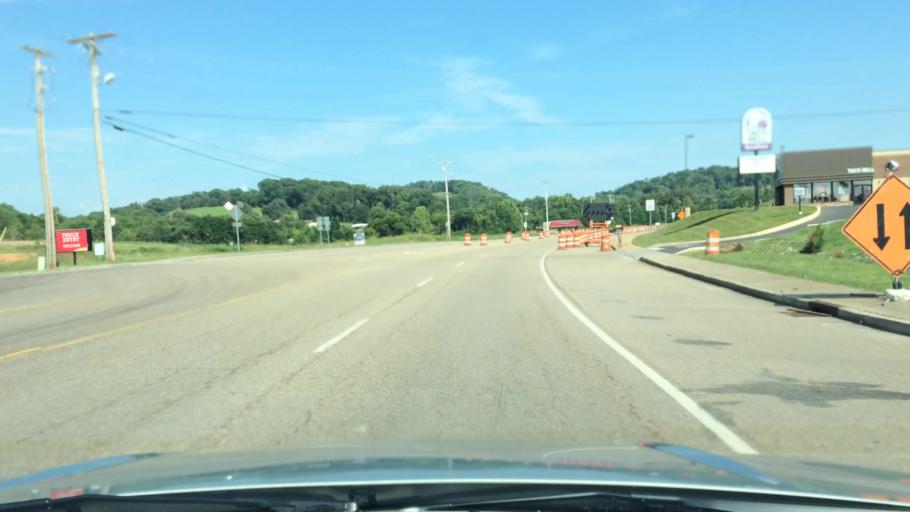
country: US
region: Tennessee
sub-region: Jefferson County
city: White Pine
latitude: 36.1096
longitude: -83.3383
